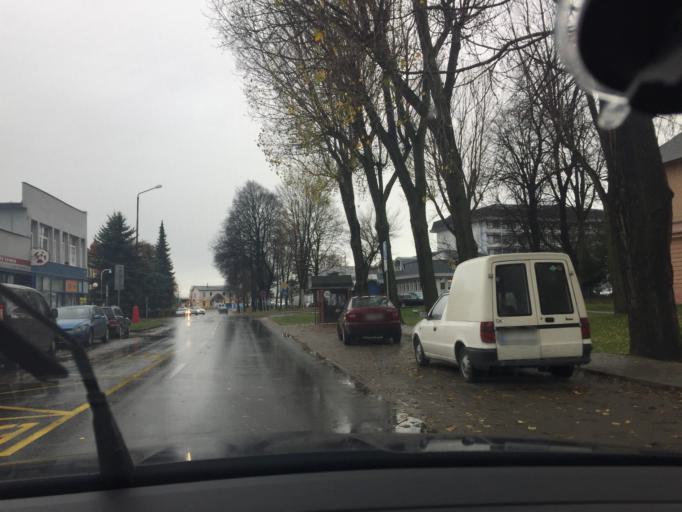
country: SK
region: Presovsky
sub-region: Okres Presov
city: Kezmarok
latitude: 49.1392
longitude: 20.4277
